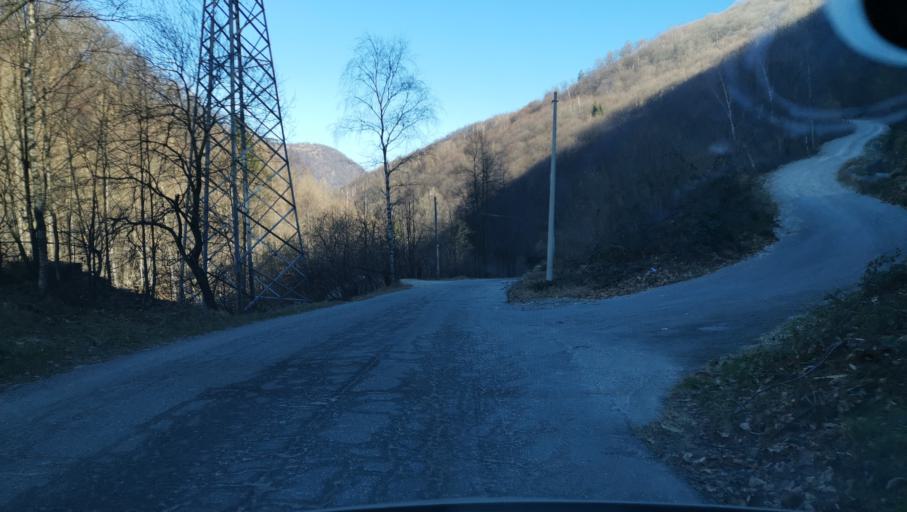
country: IT
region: Piedmont
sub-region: Provincia di Torino
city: Rora
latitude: 44.7757
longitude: 7.2063
